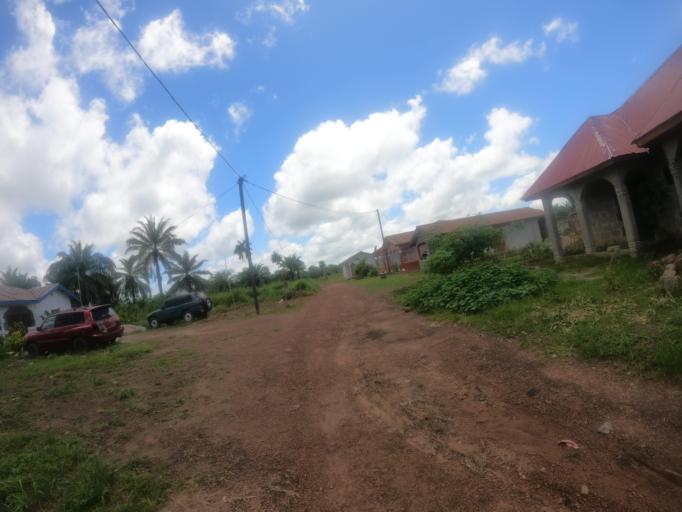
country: SL
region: Northern Province
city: Makeni
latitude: 8.8753
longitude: -12.0951
